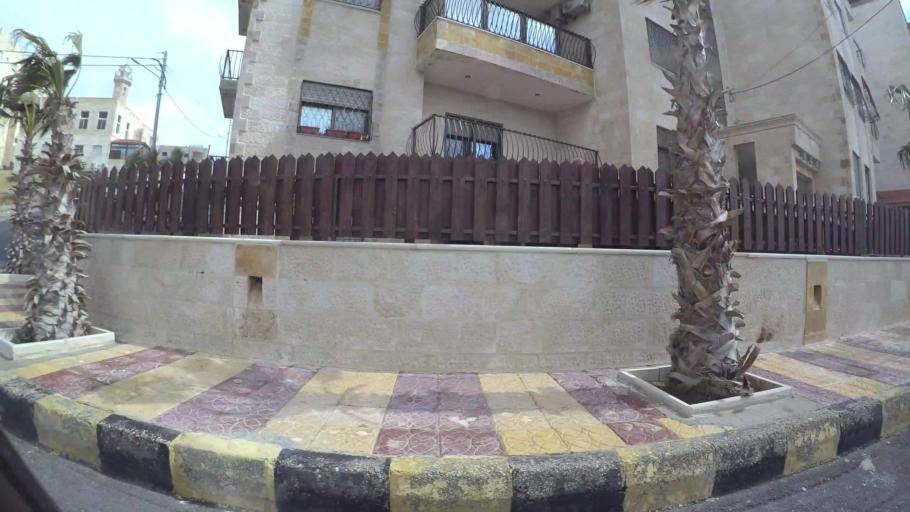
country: JO
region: Amman
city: Al Jubayhah
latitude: 32.0594
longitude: 35.8711
